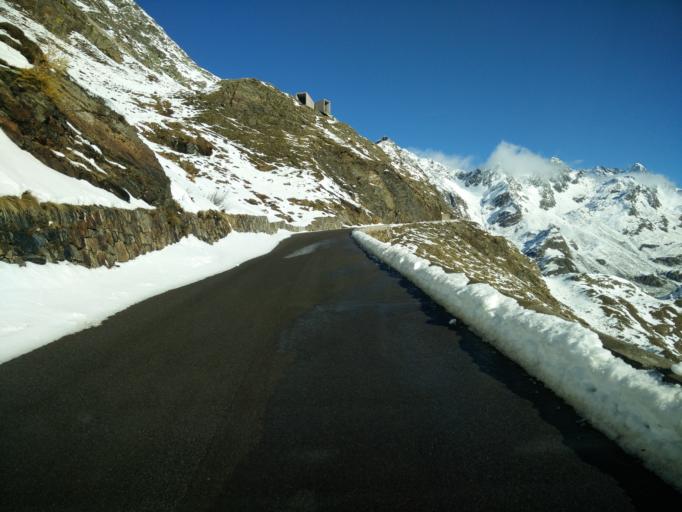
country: IT
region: Trentino-Alto Adige
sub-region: Bolzano
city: Moso in Passiria
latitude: 46.8908
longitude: 11.1206
